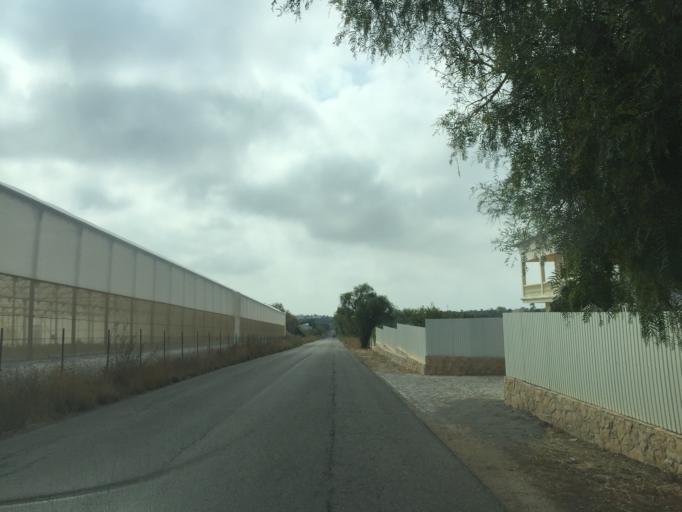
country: PT
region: Faro
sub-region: Olhao
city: Olhao
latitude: 37.0706
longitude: -7.8831
